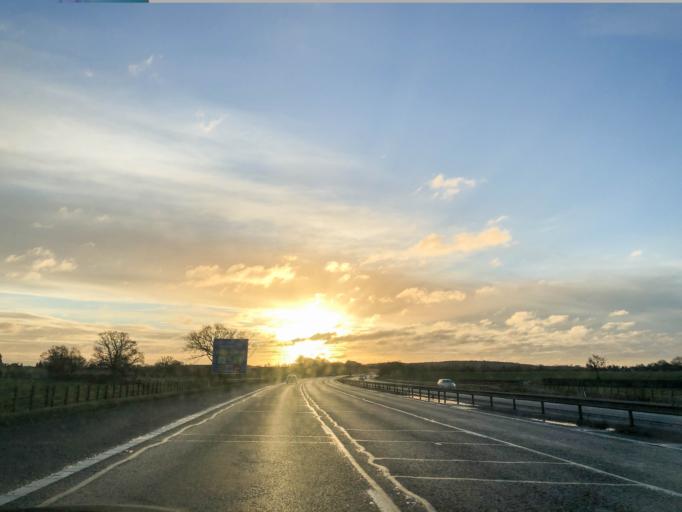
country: GB
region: England
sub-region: Warwickshire
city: Harbury
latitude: 52.2280
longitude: -1.5225
